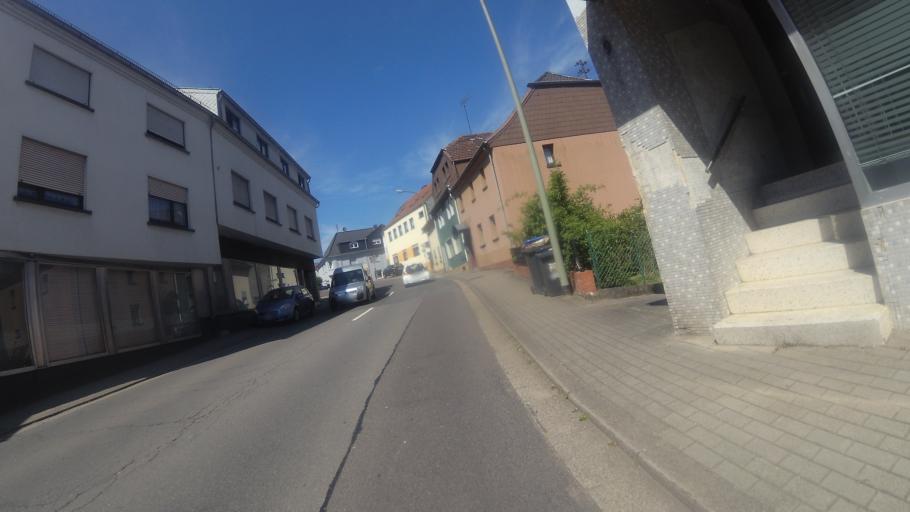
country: DE
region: Saarland
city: Quierschied
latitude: 49.3243
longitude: 7.0549
